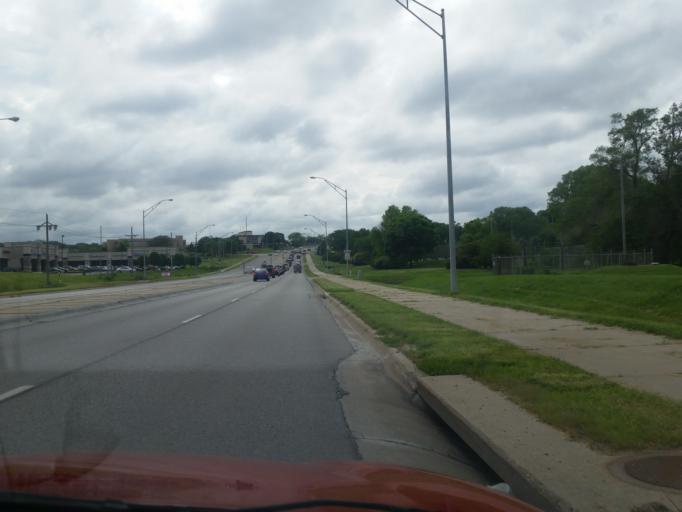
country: US
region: Nebraska
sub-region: Sarpy County
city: Offutt Air Force Base
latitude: 41.1183
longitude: -95.9417
